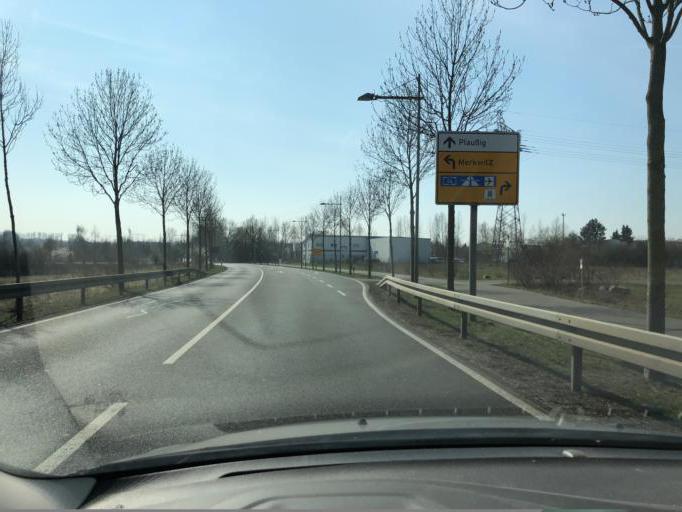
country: DE
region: Saxony
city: Taucha
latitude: 51.3988
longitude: 12.4589
